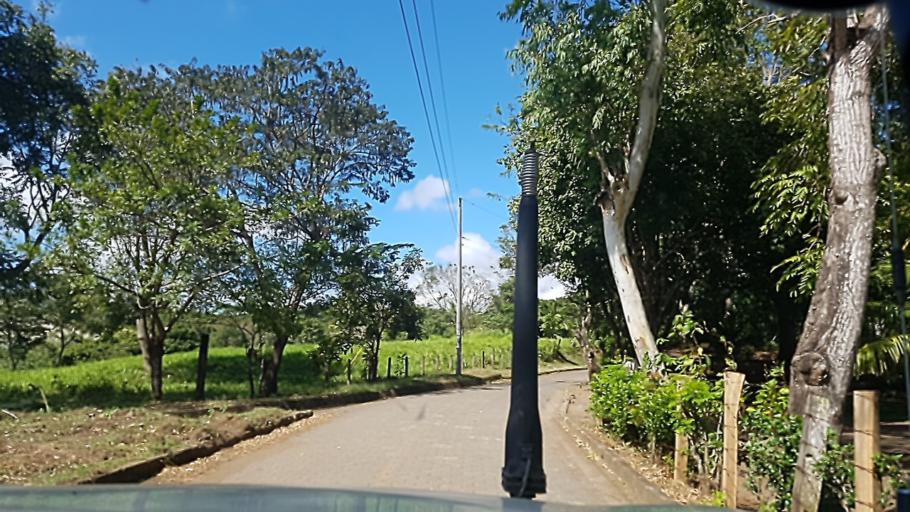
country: NI
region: Carazo
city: La Paz de Oriente
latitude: 11.8285
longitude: -86.1526
